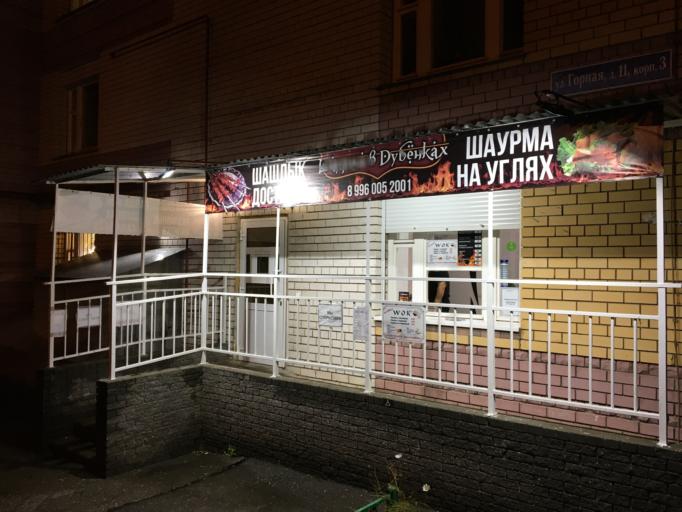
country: RU
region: Nizjnij Novgorod
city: Nizhniy Novgorod
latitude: 56.2577
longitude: 43.9812
